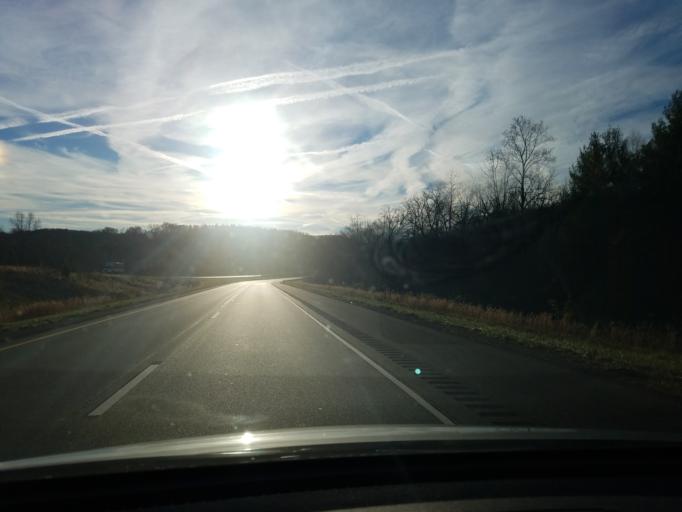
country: US
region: Indiana
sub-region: Crawford County
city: English
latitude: 38.2288
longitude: -86.6338
